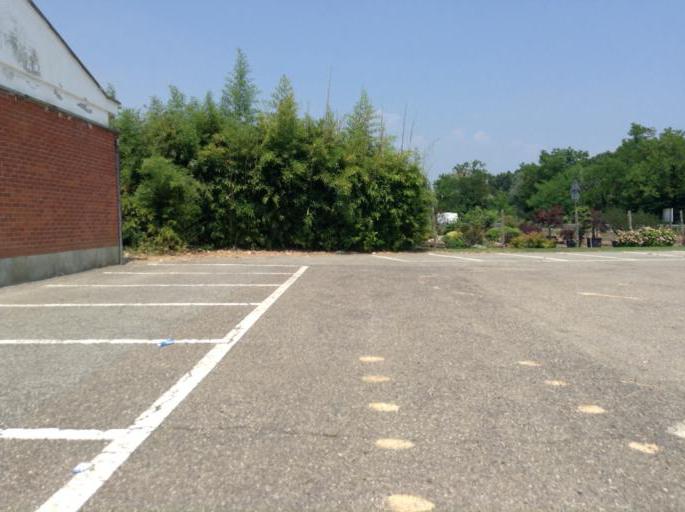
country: IT
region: Piedmont
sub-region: Provincia di Torino
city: Carignano
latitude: 44.9179
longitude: 7.6745
